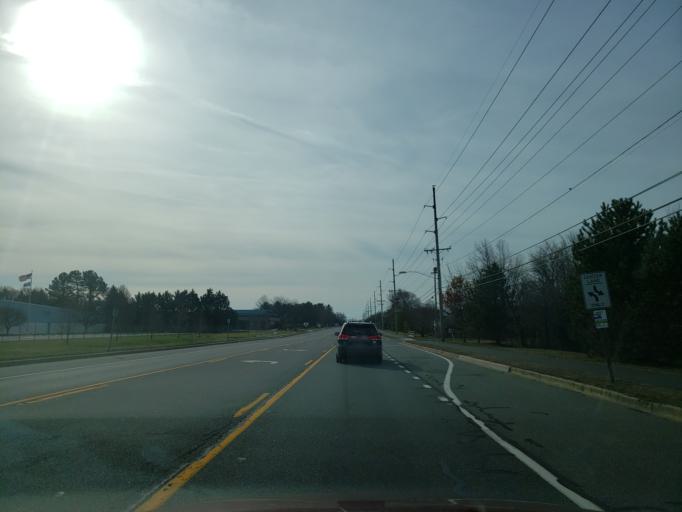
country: US
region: Delaware
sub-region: Kent County
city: Dover
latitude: 39.1667
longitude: -75.5456
